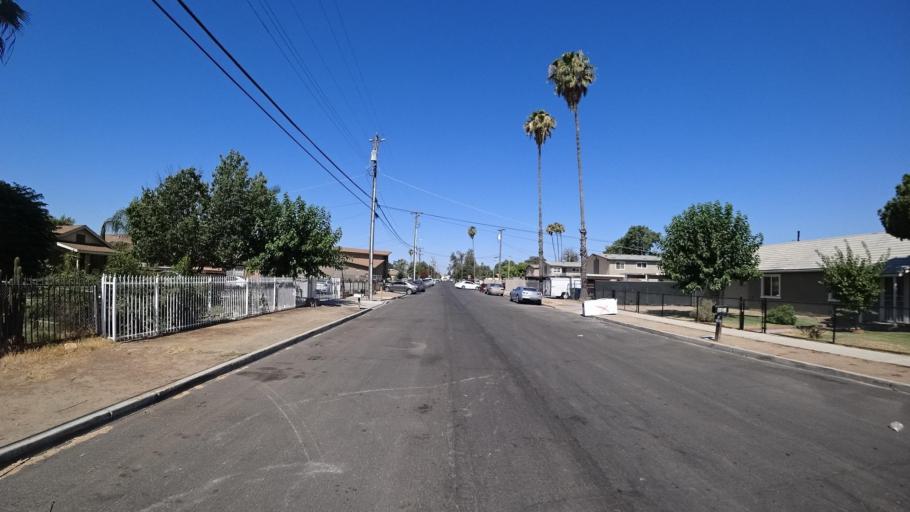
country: US
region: California
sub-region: Fresno County
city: Fresno
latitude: 36.7595
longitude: -119.7508
